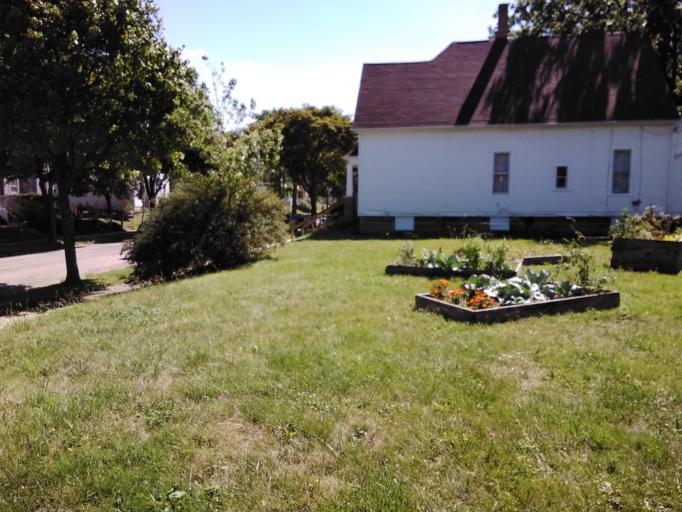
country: US
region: Wisconsin
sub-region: Milwaukee County
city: Milwaukee
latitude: 43.0728
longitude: -87.9370
